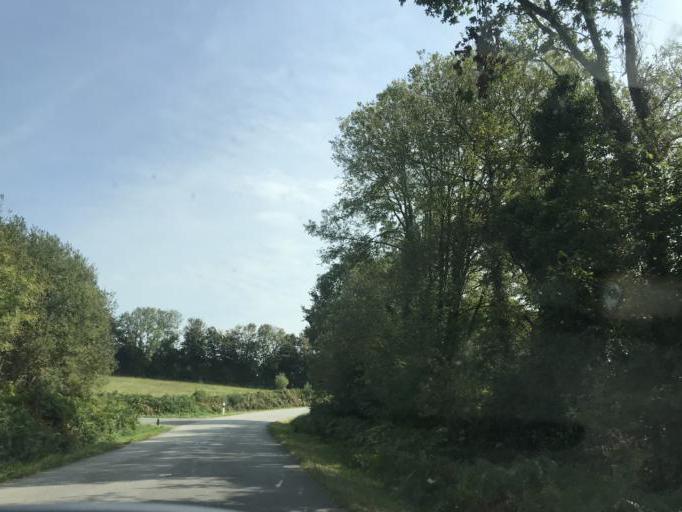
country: FR
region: Brittany
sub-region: Departement du Finistere
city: Loperec
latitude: 48.2962
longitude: -4.0656
